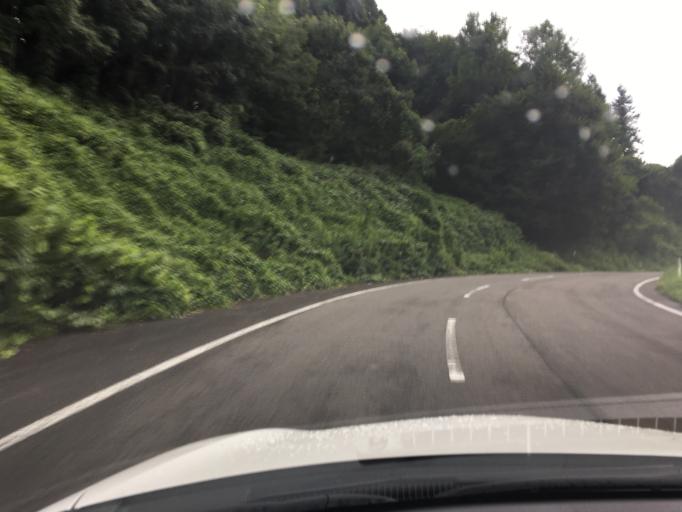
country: JP
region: Fukushima
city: Funehikimachi-funehiki
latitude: 37.4229
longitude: 140.5478
